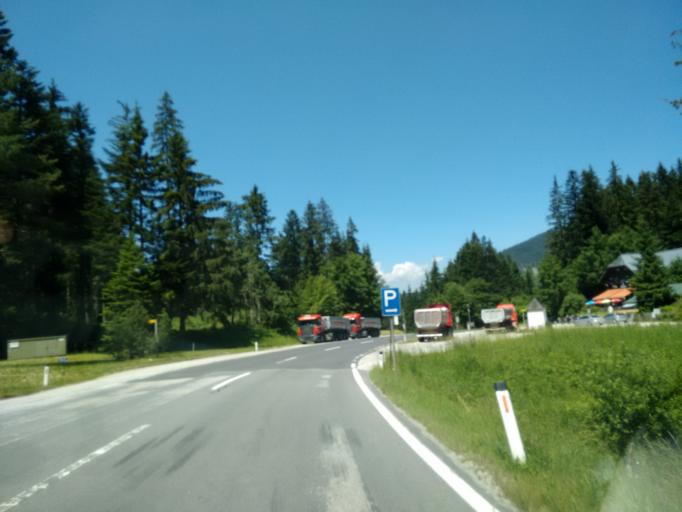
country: AT
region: Styria
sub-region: Politischer Bezirk Liezen
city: Altaussee
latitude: 47.6225
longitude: 13.6941
